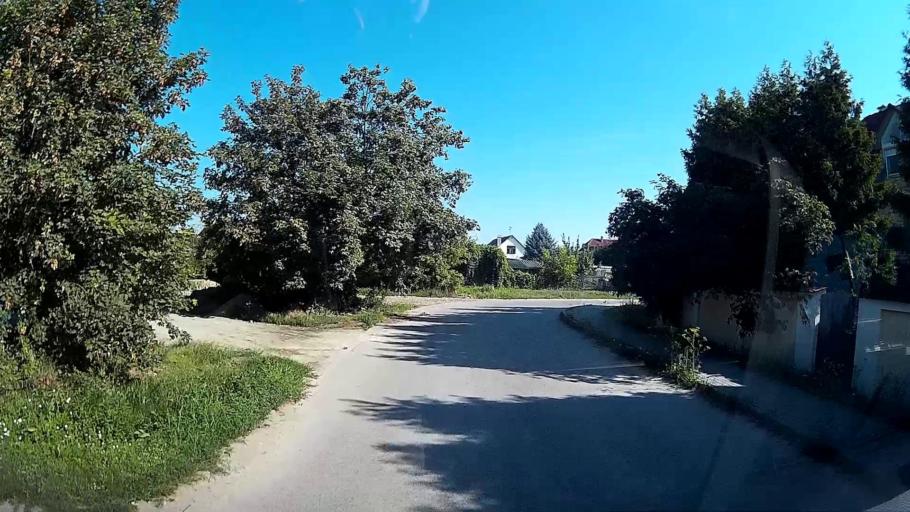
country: HU
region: Pest
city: Leanyfalu
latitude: 47.7155
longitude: 19.0987
